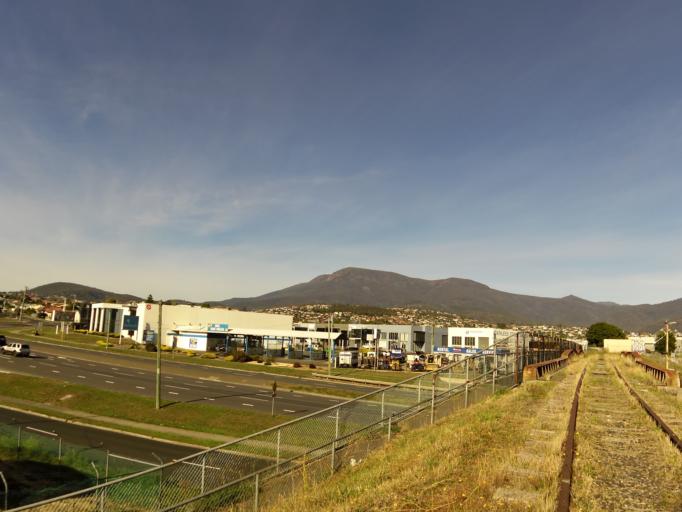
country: AU
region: Tasmania
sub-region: Glenorchy
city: Lutana
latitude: -42.8368
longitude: 147.3030
